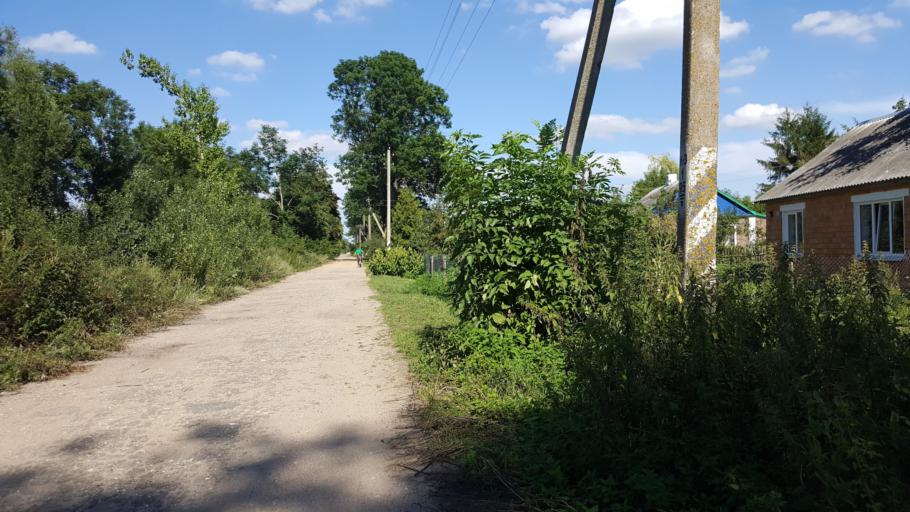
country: BY
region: Brest
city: Charnawchytsy
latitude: 52.3244
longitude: 23.6285
